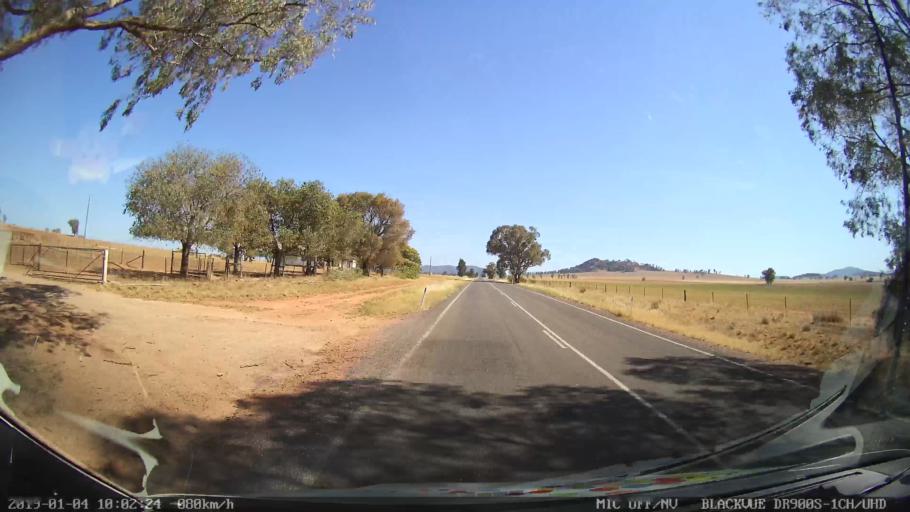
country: AU
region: New South Wales
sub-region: Cabonne
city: Canowindra
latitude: -33.4767
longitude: 148.3655
